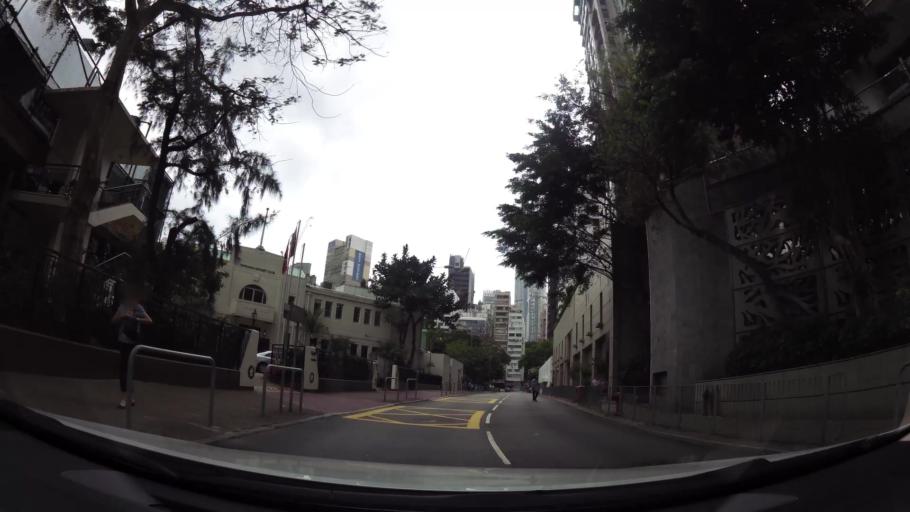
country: HK
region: Kowloon City
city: Kowloon
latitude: 22.3052
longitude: 114.1734
